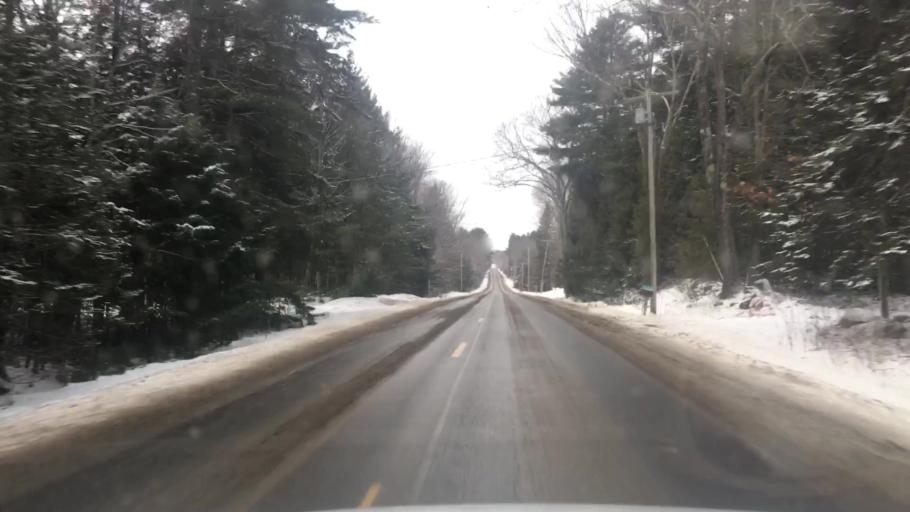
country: US
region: Maine
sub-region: Waldo County
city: Searsmont
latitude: 44.3731
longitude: -69.2071
